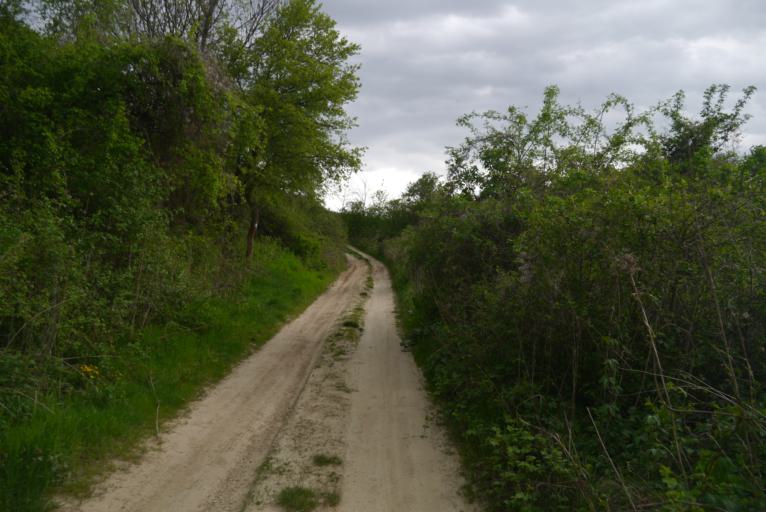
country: HU
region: Komarom-Esztergom
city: Piliscsev
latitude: 47.6733
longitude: 18.8313
